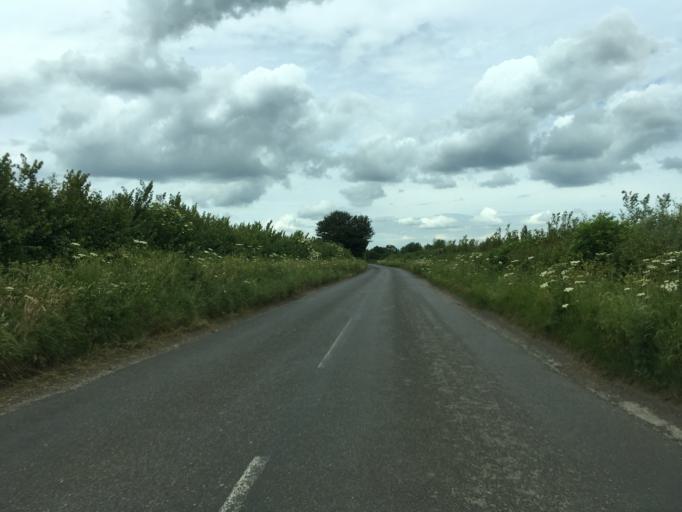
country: GB
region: England
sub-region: Wiltshire
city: Norton
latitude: 51.5377
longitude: -2.1403
